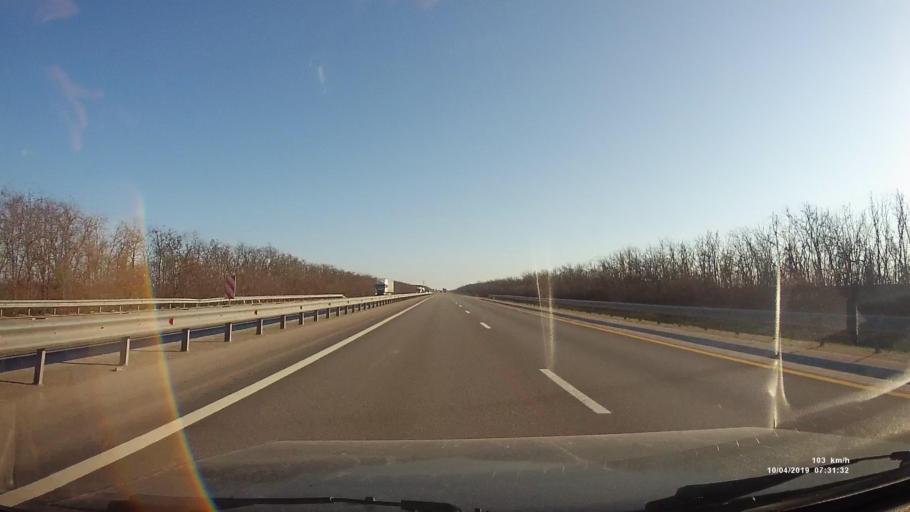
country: RU
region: Rostov
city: Zverevo
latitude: 47.9862
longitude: 40.2214
